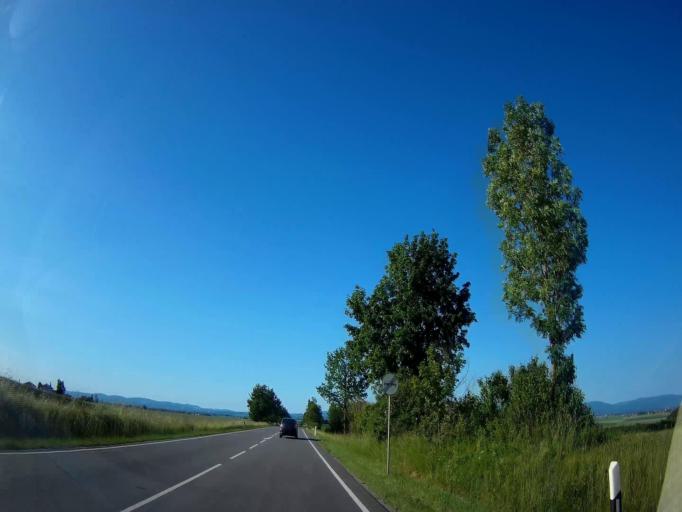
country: DE
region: Bavaria
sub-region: Lower Bavaria
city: Oberschneiding
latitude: 48.7891
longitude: 12.6505
